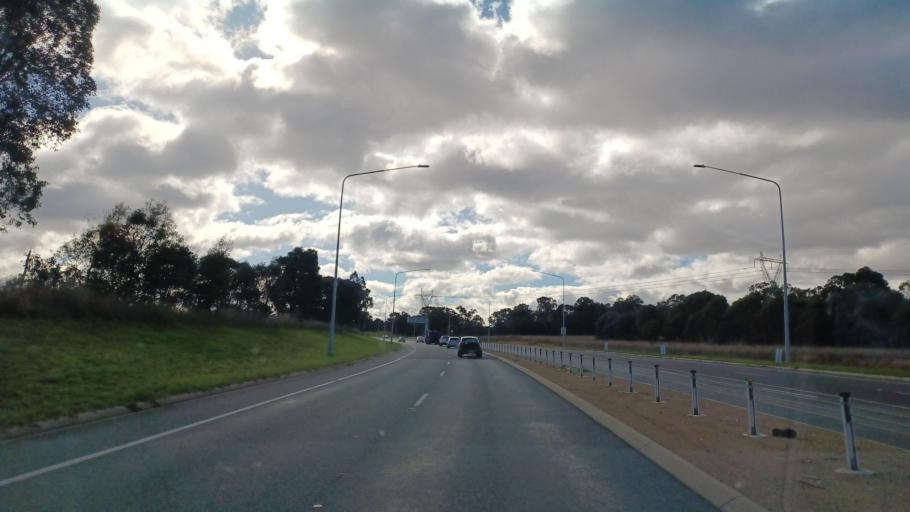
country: AU
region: Australian Capital Territory
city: Kaleen
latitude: -35.2225
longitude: 149.1285
